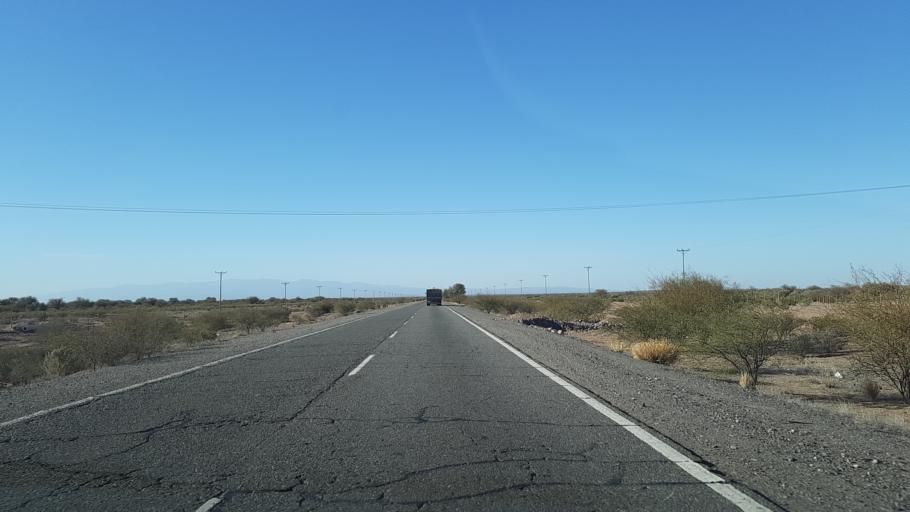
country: AR
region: San Juan
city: Caucete
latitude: -31.6579
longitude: -67.7731
